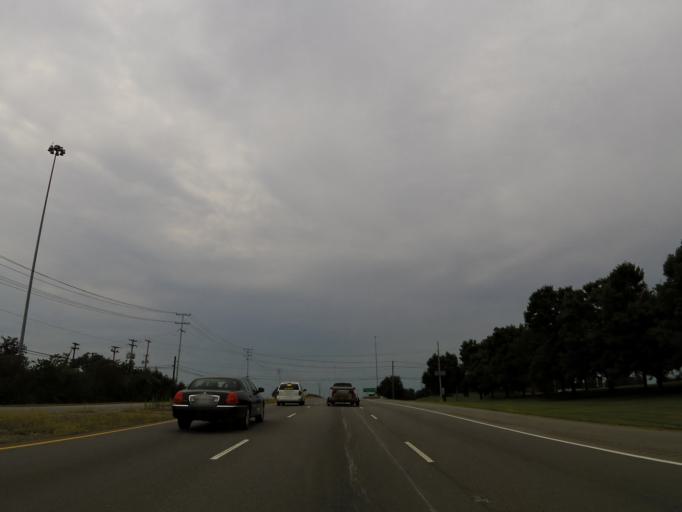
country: US
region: Tennessee
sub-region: Knox County
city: Knoxville
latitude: 35.9395
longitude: -83.9486
